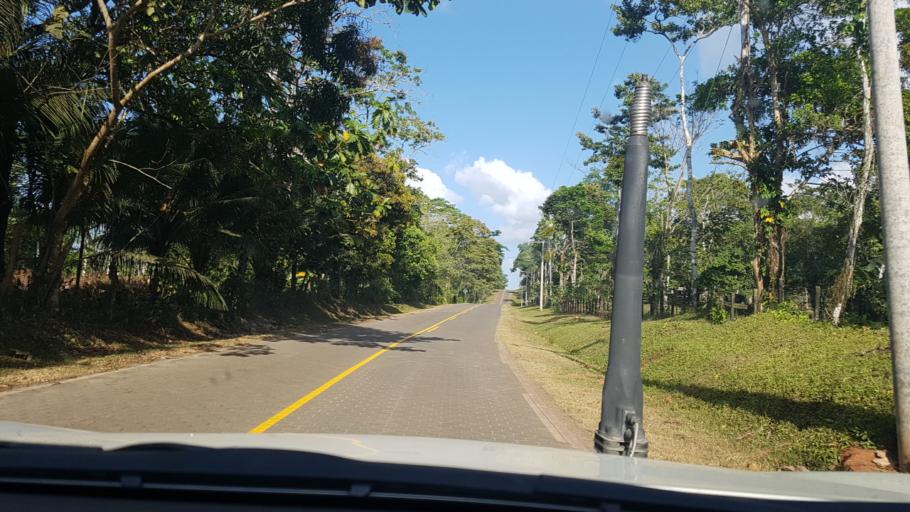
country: NI
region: Atlantico Sur
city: Nueva Guinea
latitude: 11.6884
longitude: -84.4314
